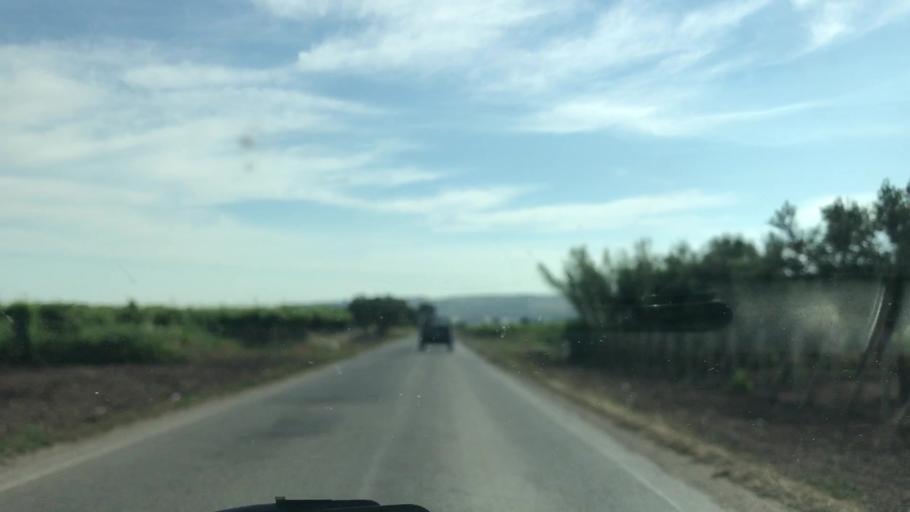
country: IT
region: Apulia
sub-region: Provincia di Taranto
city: San Giorgio Ionico
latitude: 40.4365
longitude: 17.3503
